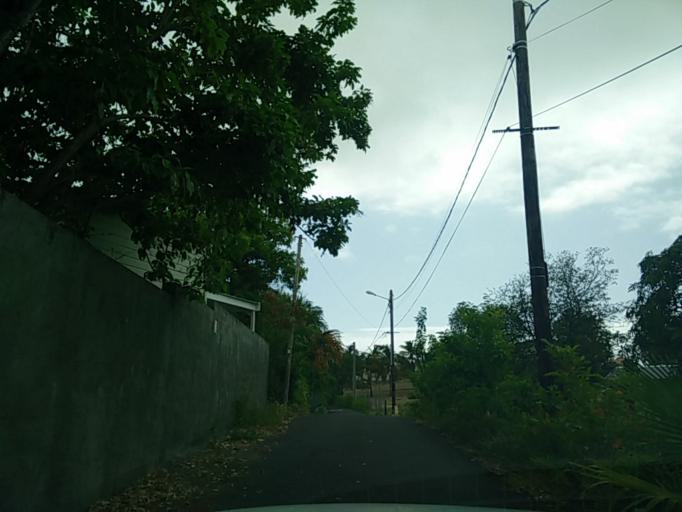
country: GP
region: Guadeloupe
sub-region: Guadeloupe
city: Sainte-Anne
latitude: 16.2201
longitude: -61.4013
